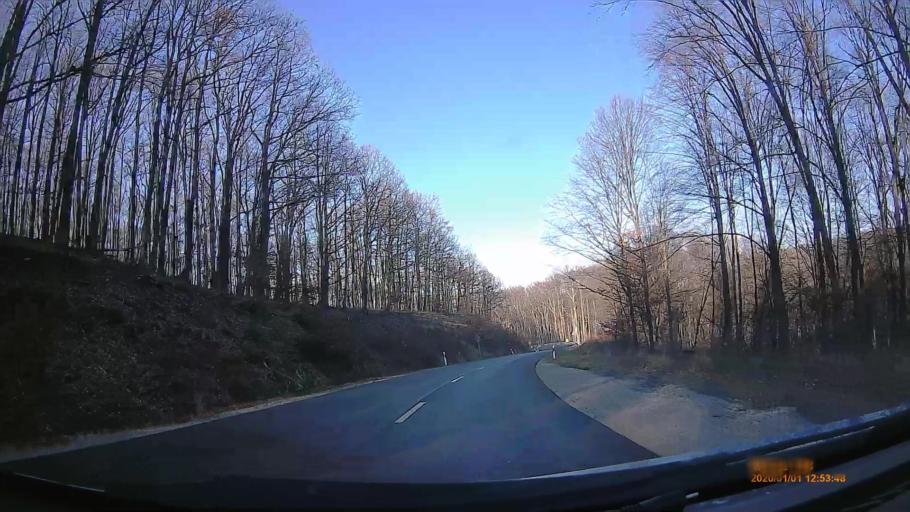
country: HU
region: Heves
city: Paradsasvar
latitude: 47.9061
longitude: 19.9924
